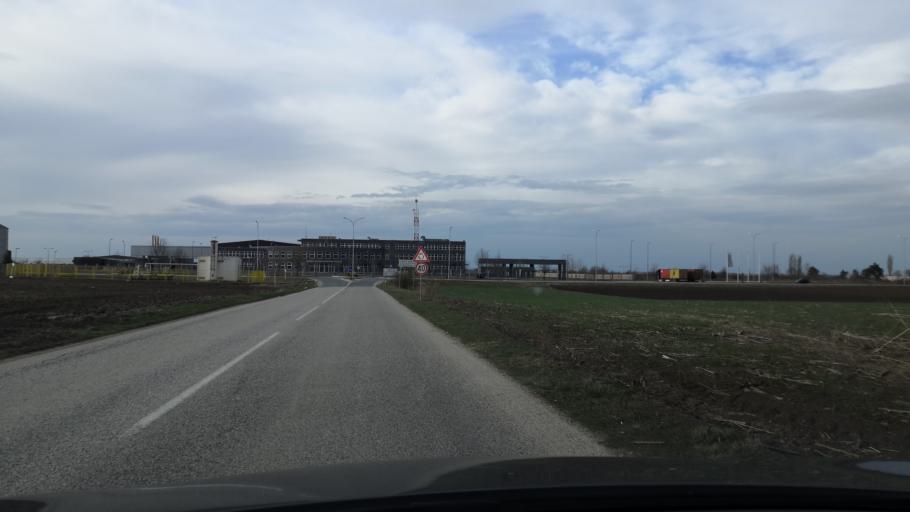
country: RS
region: Autonomna Pokrajina Vojvodina
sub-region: Sremski Okrug
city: Ingija
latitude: 45.0542
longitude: 20.1041
